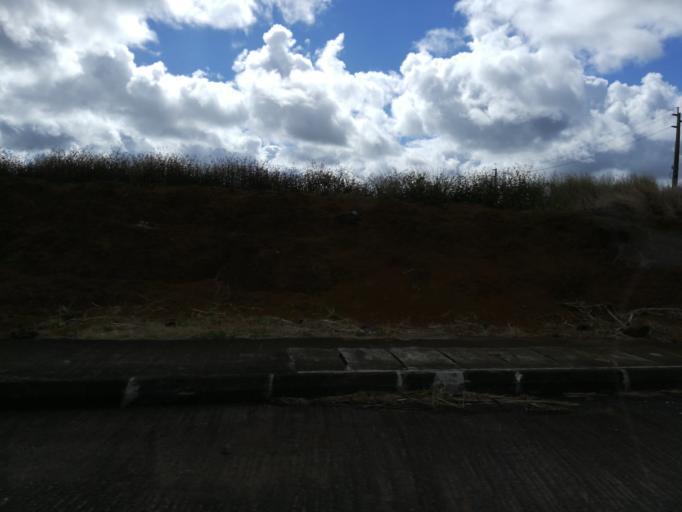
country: MU
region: Grand Port
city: Plaine Magnien
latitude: -20.4191
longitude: 57.6678
